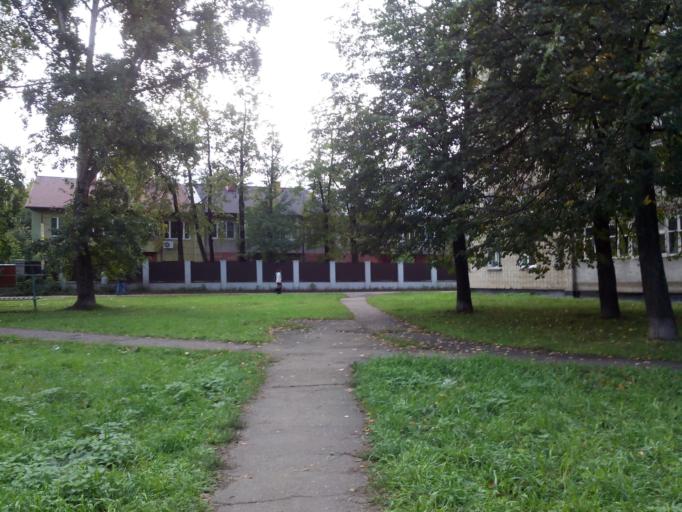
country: RU
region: Udmurtiya
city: Glazov
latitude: 58.1347
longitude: 52.6864
